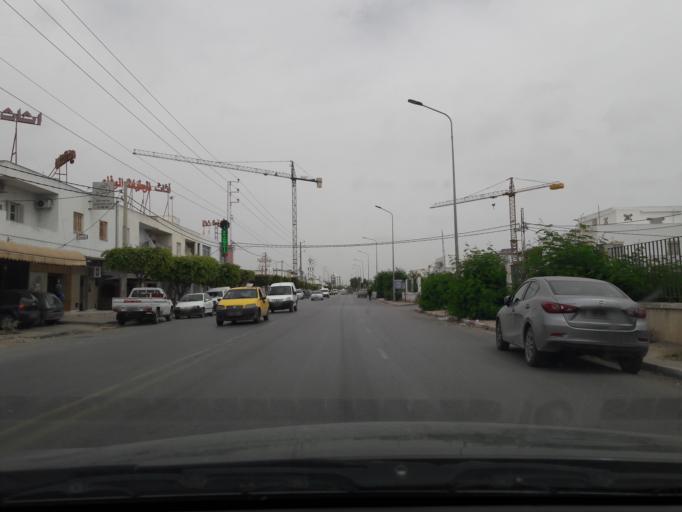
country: TN
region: Safaqis
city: Al Qarmadah
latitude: 34.7847
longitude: 10.7603
